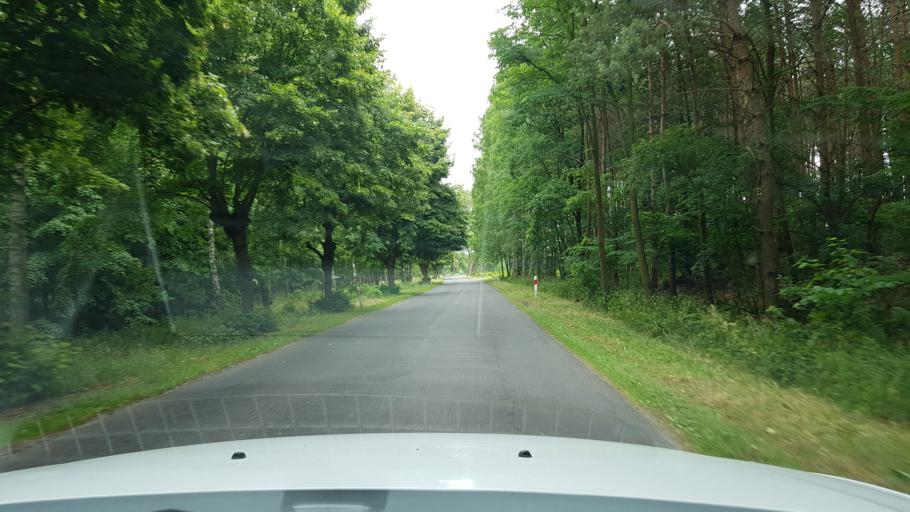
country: PL
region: West Pomeranian Voivodeship
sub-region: Powiat mysliborski
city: Boleszkowice
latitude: 52.6832
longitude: 14.6182
